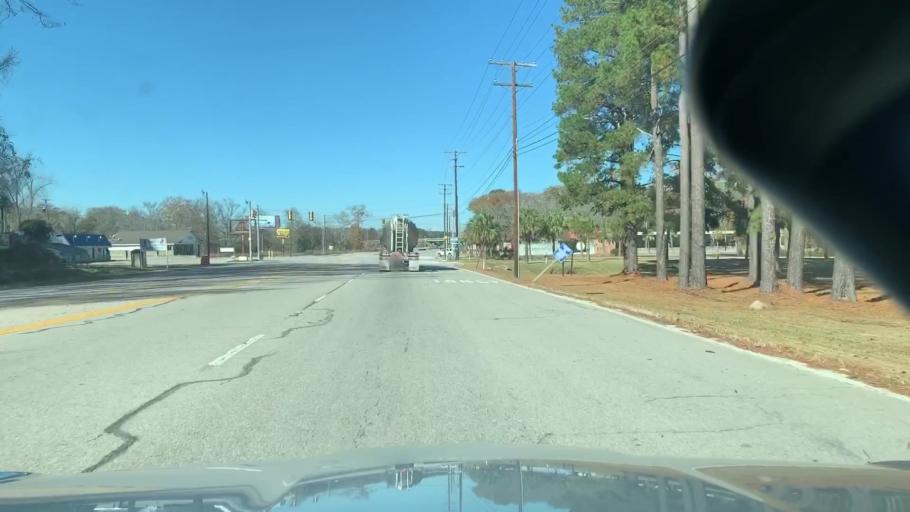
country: US
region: South Carolina
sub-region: Richland County
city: Columbia
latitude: 33.9445
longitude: -80.9866
